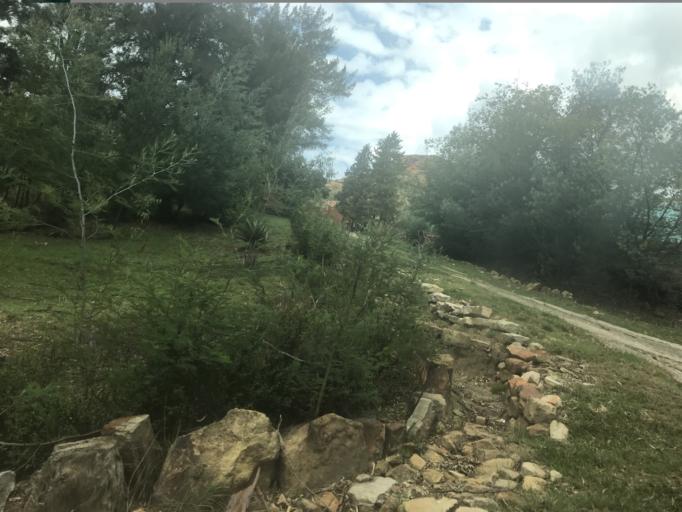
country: LS
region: Maseru
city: Nako
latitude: -29.6314
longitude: 27.5088
